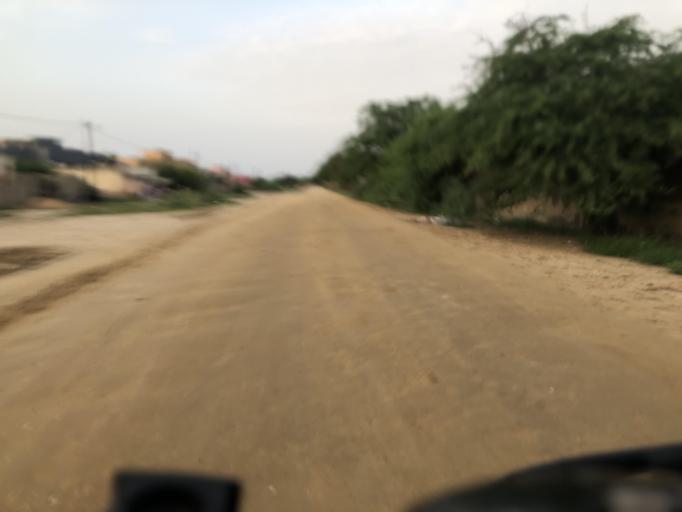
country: SN
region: Saint-Louis
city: Saint-Louis
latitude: 16.0524
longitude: -16.4327
